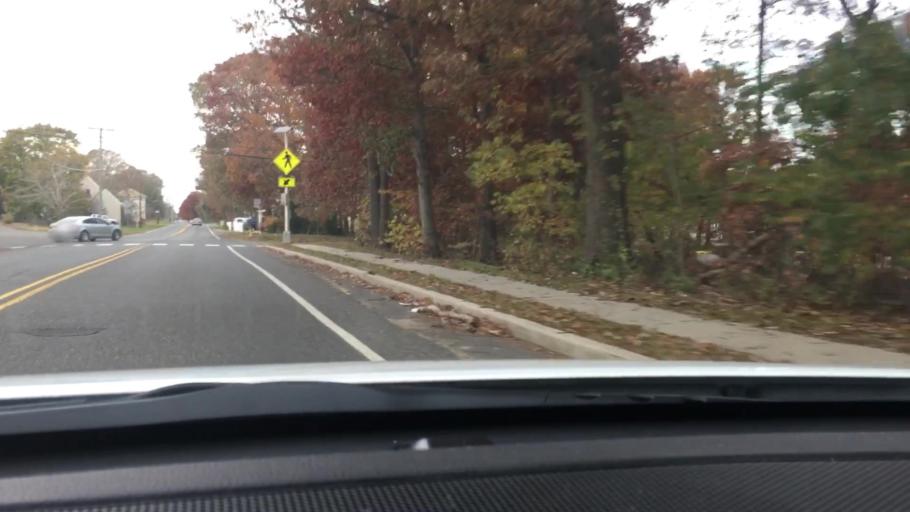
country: US
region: New Jersey
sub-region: Atlantic County
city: Northfield
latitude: 39.3869
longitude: -74.5468
